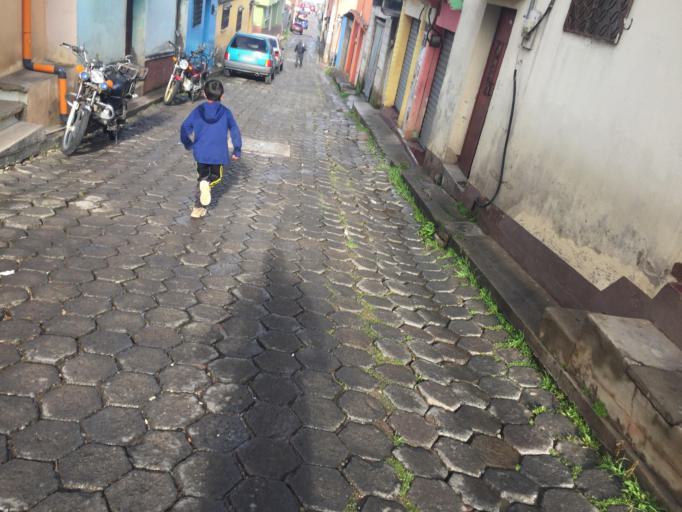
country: GT
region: Totonicapan
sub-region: Municipio de Totonicapan
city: Totonicapan
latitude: 14.9122
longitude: -91.3571
